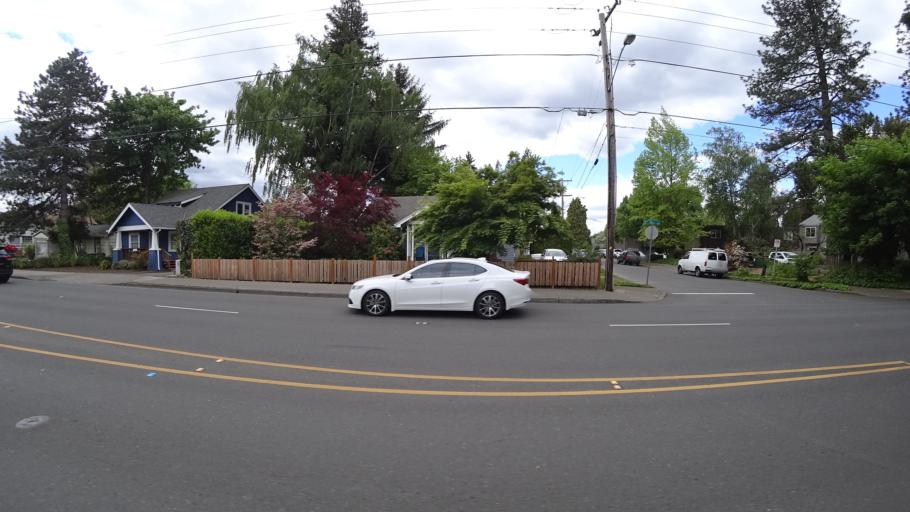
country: US
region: Oregon
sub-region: Washington County
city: Beaverton
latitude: 45.4775
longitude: -122.8056
